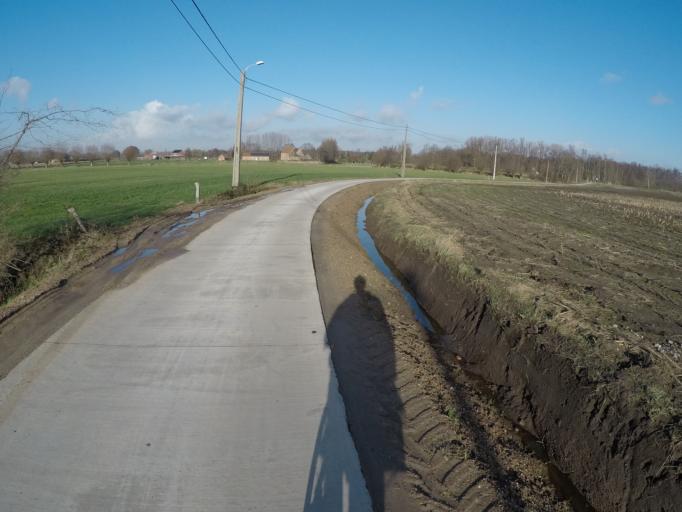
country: BE
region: Flanders
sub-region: Provincie Antwerpen
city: Ranst
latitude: 51.2109
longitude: 4.5719
